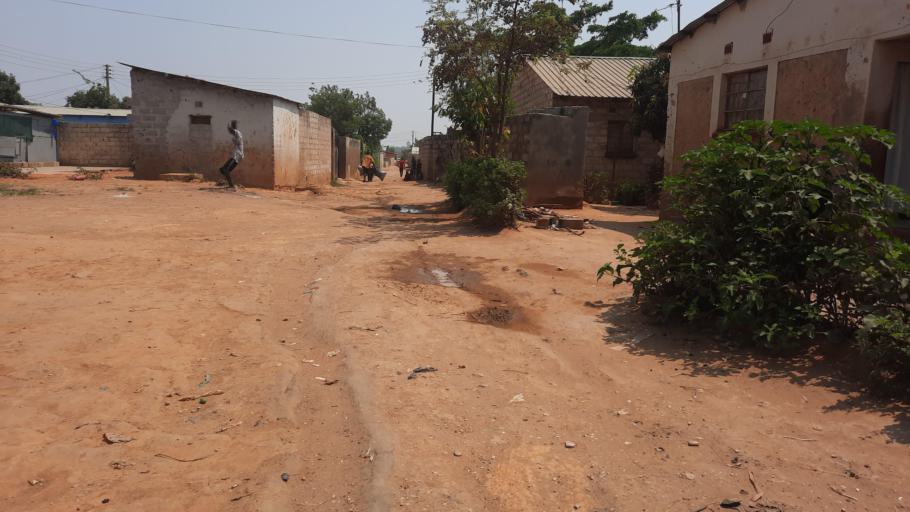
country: ZM
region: Lusaka
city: Lusaka
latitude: -15.3947
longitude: 28.3802
